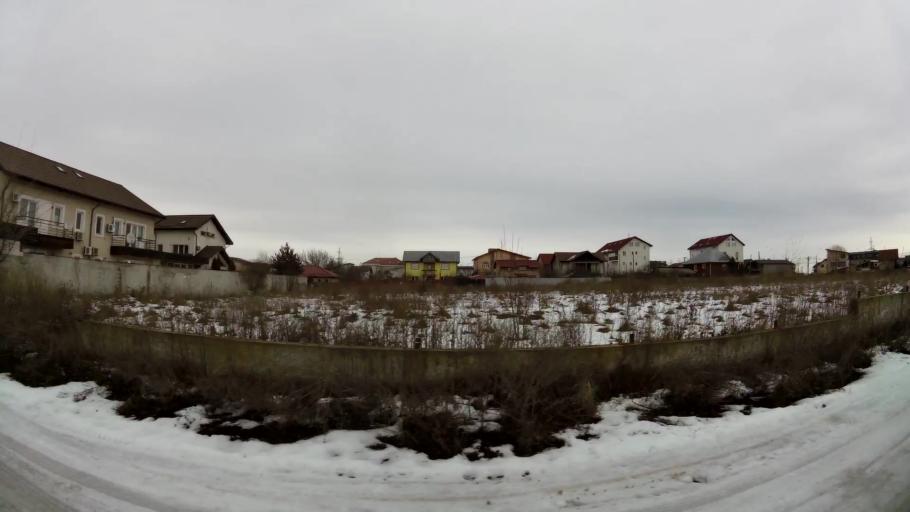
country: RO
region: Ilfov
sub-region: Comuna Pantelimon
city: Pantelimon
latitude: 44.4546
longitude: 26.2184
